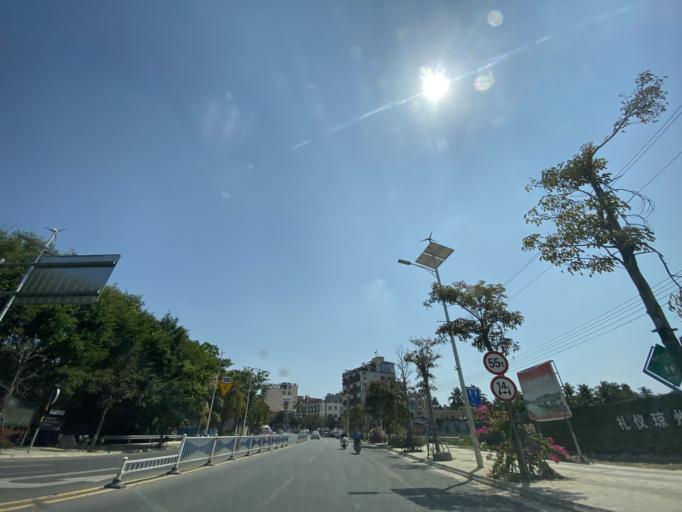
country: CN
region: Hainan
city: Yingzhou
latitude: 18.4228
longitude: 109.8464
